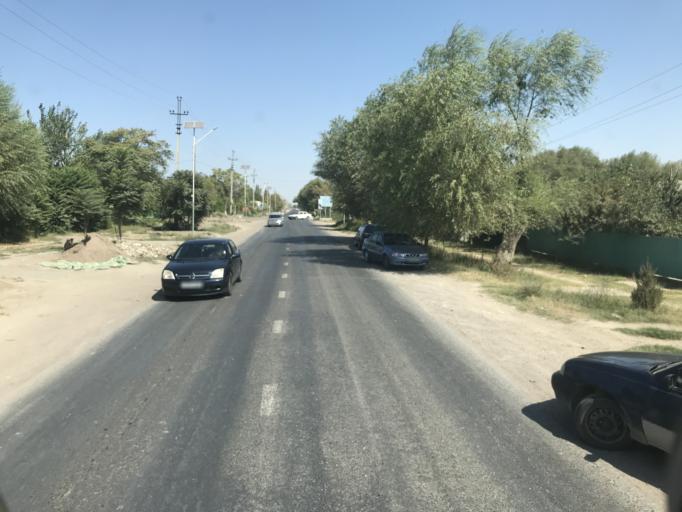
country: KZ
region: Ongtustik Qazaqstan
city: Ilyich
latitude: 40.9336
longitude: 68.4883
